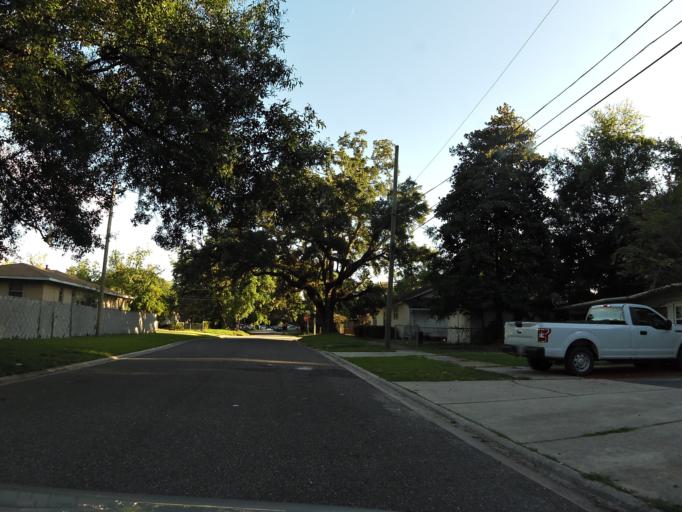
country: US
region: Florida
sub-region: Duval County
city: Jacksonville
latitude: 30.3601
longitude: -81.7023
